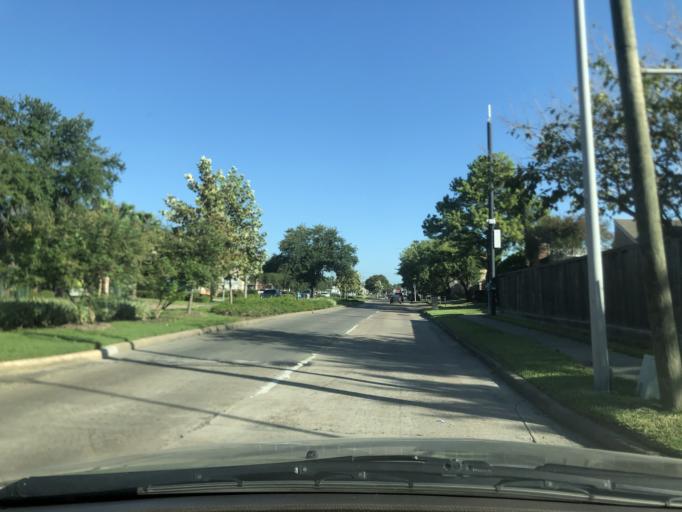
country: US
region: Texas
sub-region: Harris County
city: Bunker Hill Village
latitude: 29.7452
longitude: -95.5719
